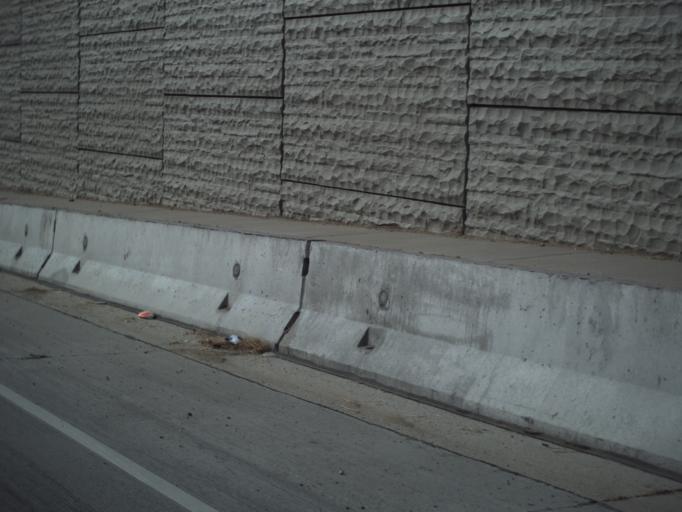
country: US
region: Utah
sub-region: Utah County
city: Lehi
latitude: 40.4322
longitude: -111.8721
